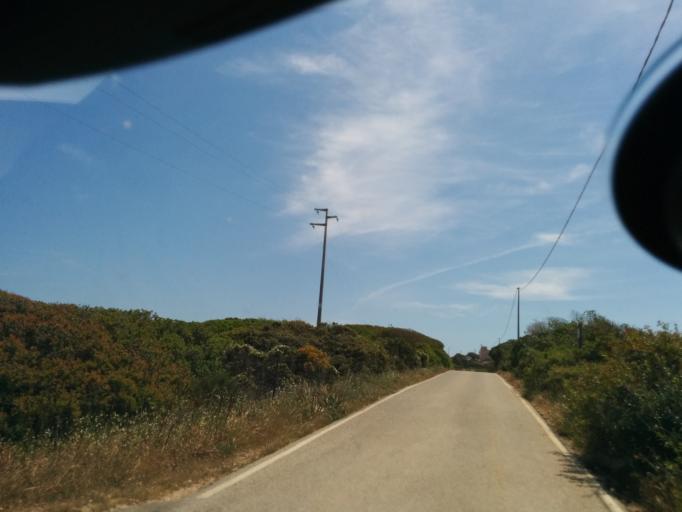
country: IT
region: Sardinia
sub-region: Provincia di Carbonia-Iglesias
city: Sant'Antioco
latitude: 39.0191
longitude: 8.3803
